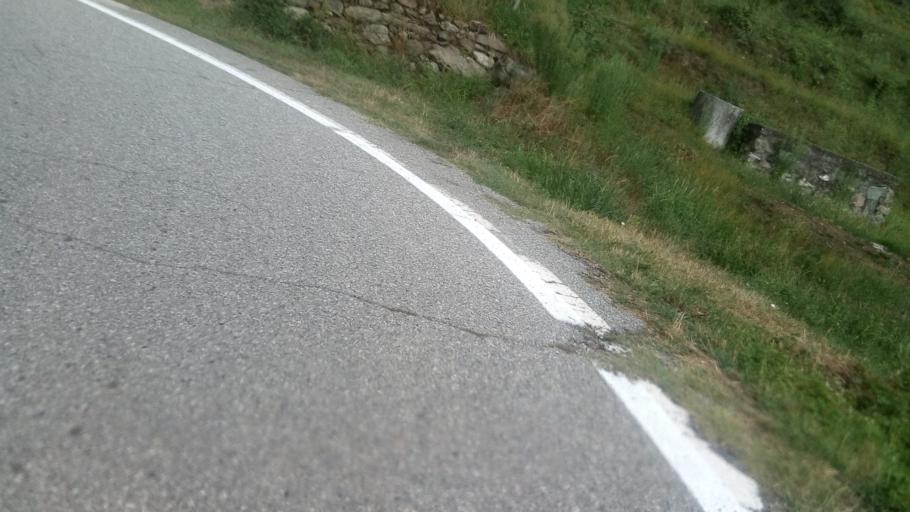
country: IT
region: Piedmont
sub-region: Provincia di Torino
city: Colleretto Giacosa
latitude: 45.4415
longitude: 7.7999
